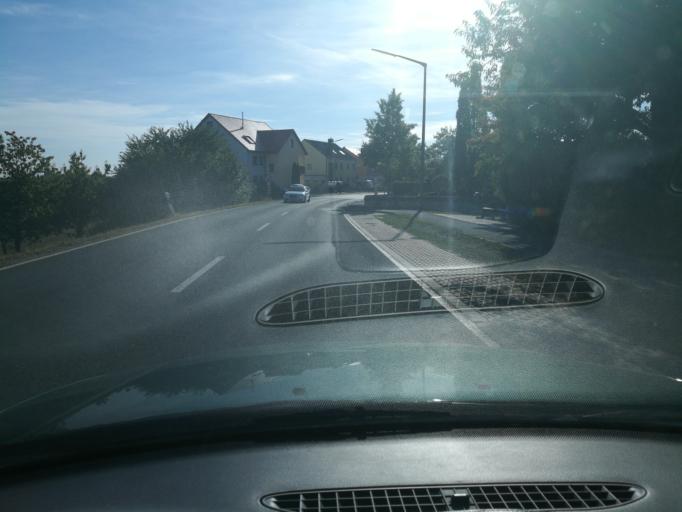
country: DE
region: Bavaria
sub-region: Regierungsbezirk Mittelfranken
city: Kalchreuth
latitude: 49.5582
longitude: 11.1427
